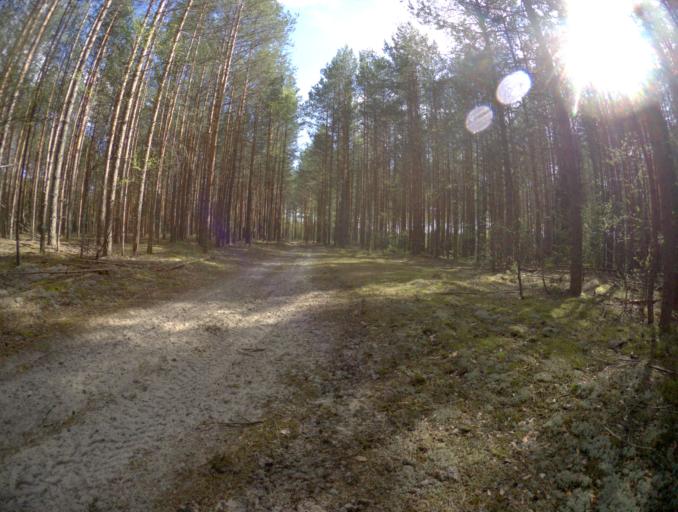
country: RU
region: Vladimir
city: Golovino
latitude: 55.8904
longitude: 40.3878
